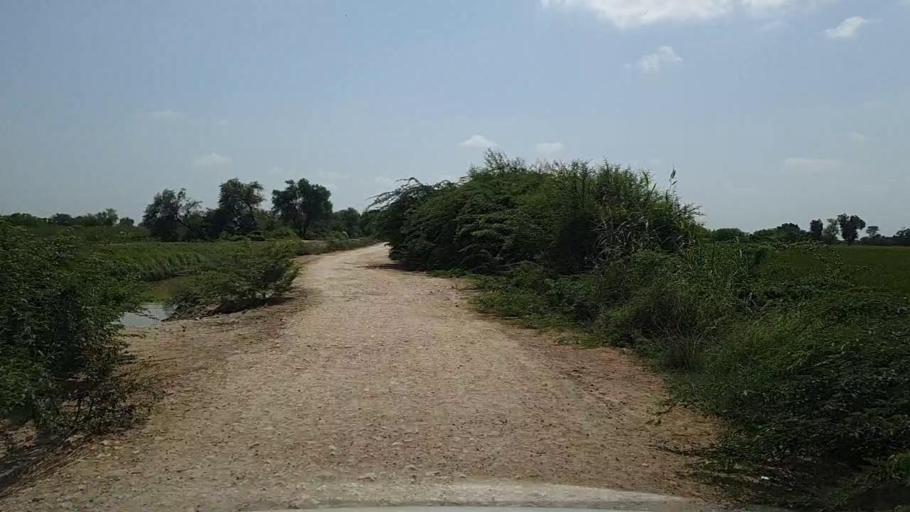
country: PK
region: Sindh
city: Kario
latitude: 24.8614
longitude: 68.6868
